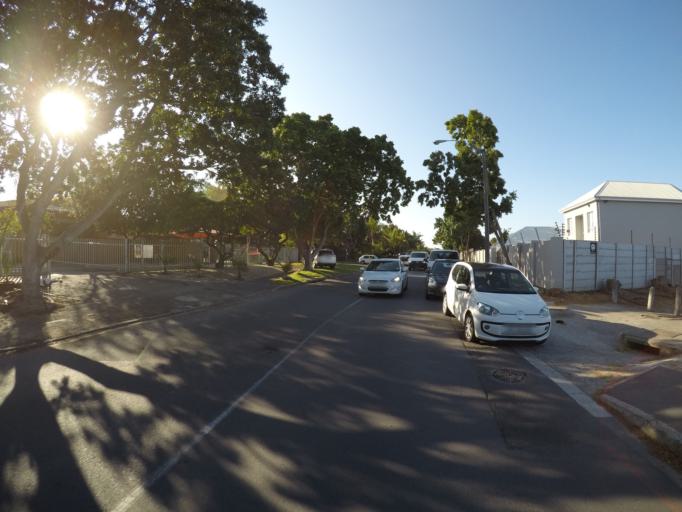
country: ZA
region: Western Cape
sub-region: City of Cape Town
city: Kraaifontein
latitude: -33.8527
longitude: 18.6574
